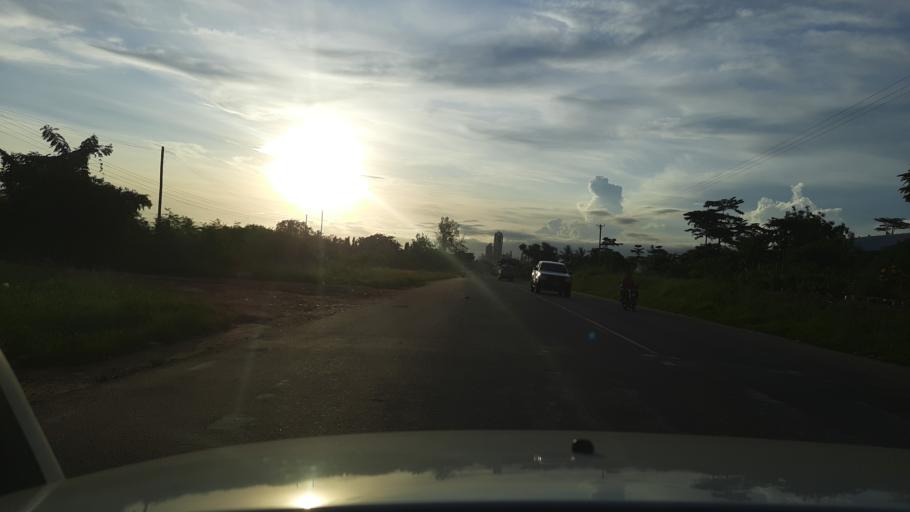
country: TZ
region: Tanga
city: Tanga
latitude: -5.1011
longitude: 39.0414
